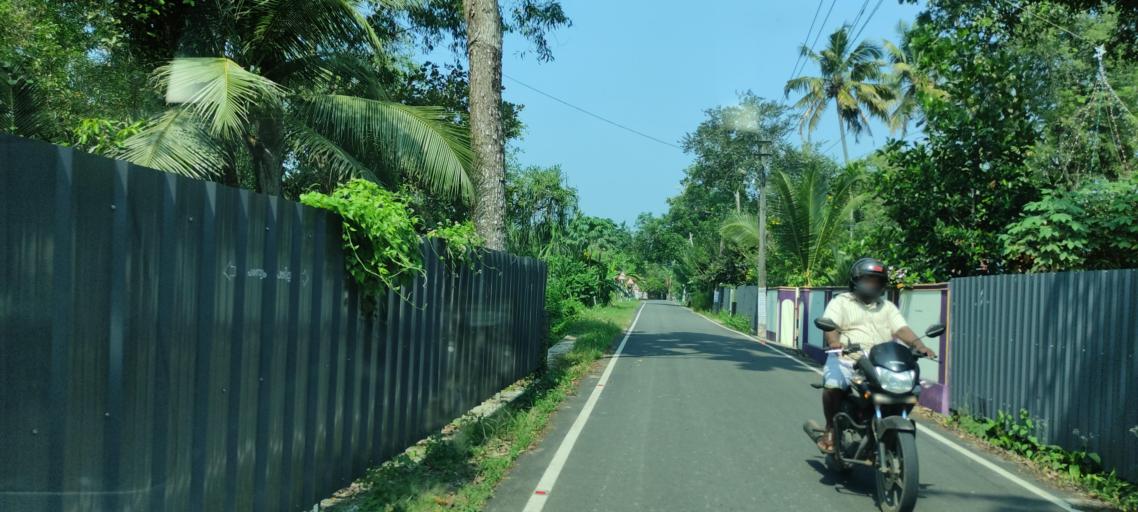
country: IN
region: Kerala
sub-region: Alappuzha
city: Alleppey
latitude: 9.5524
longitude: 76.3195
